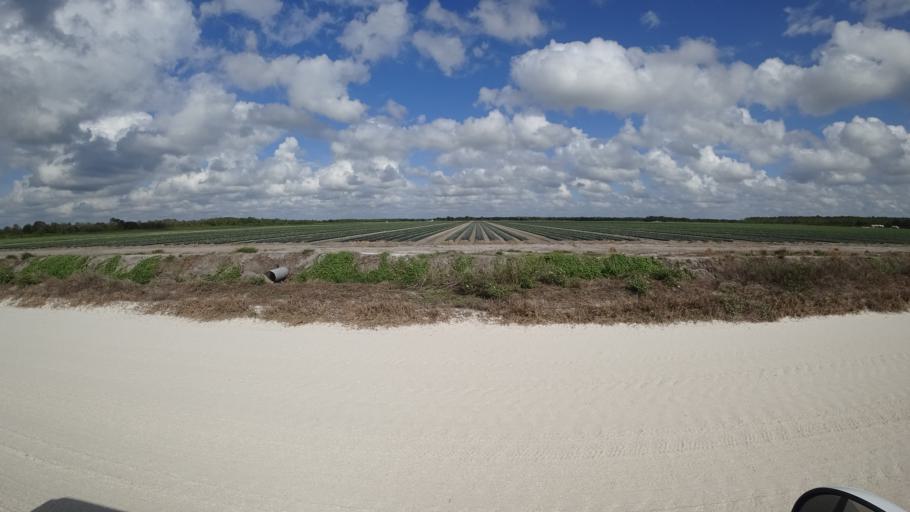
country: US
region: Florida
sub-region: Sarasota County
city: Lake Sarasota
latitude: 27.4133
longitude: -82.1936
